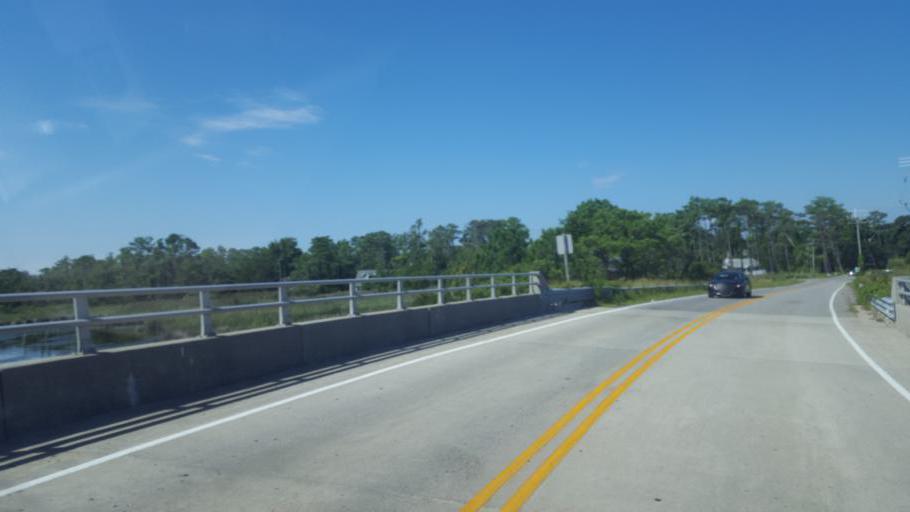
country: US
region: North Carolina
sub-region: Dare County
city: Kill Devil Hills
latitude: 36.0093
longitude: -75.6999
